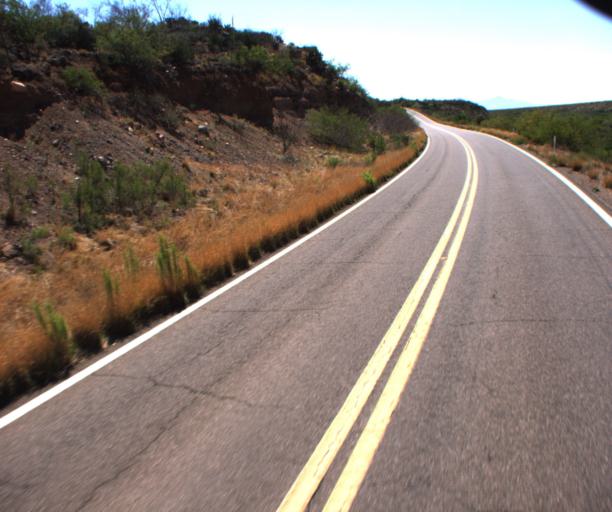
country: US
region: Arizona
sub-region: Cochise County
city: Douglas
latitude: 31.4625
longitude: -109.3810
